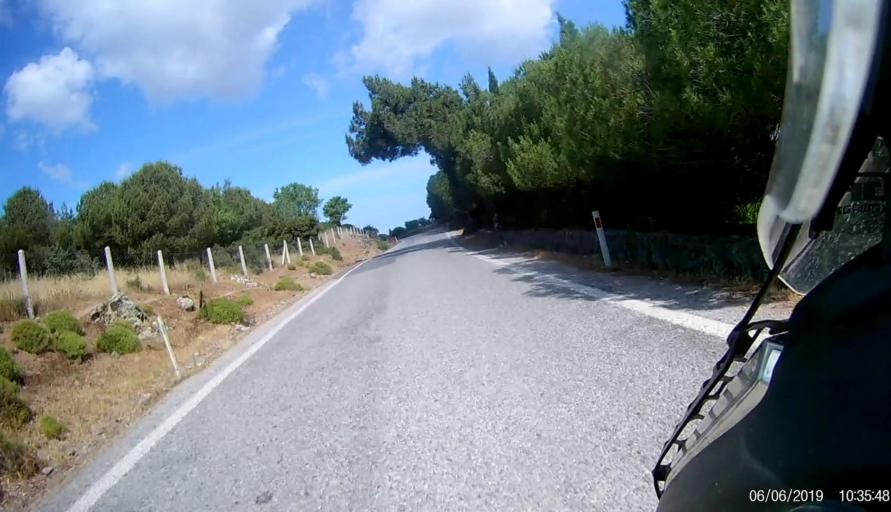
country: TR
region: Canakkale
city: Ayvacik
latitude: 39.5263
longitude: 26.4792
